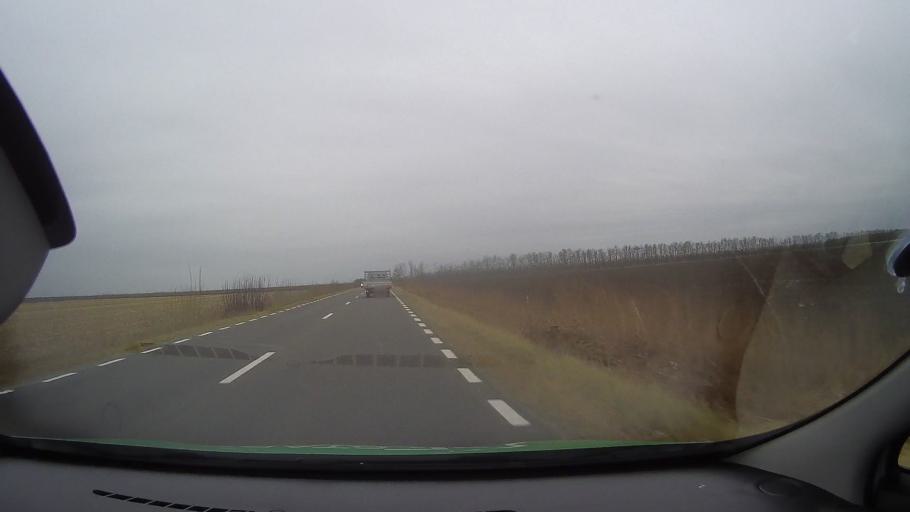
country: RO
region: Ialomita
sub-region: Comuna Scanteia
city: Iazu
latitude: 44.6856
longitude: 27.4187
